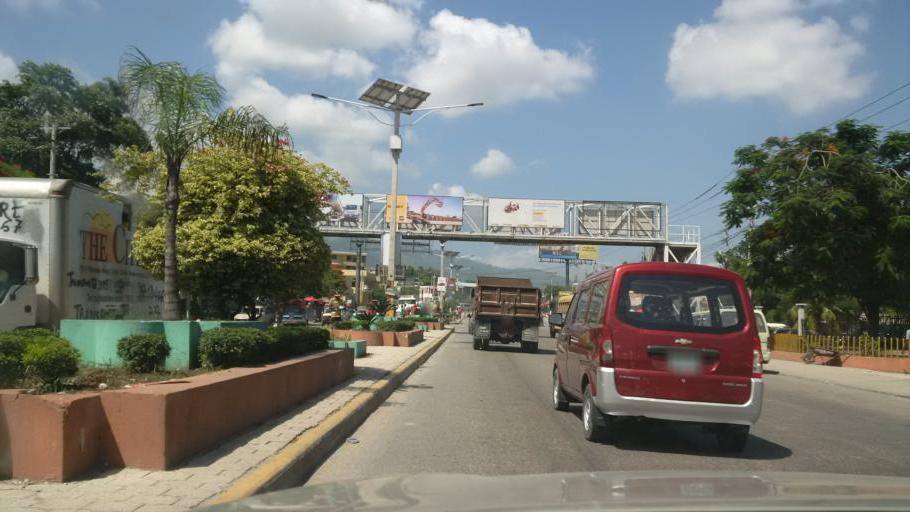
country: HT
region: Ouest
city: Delmas 73
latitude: 18.5609
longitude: -72.3177
